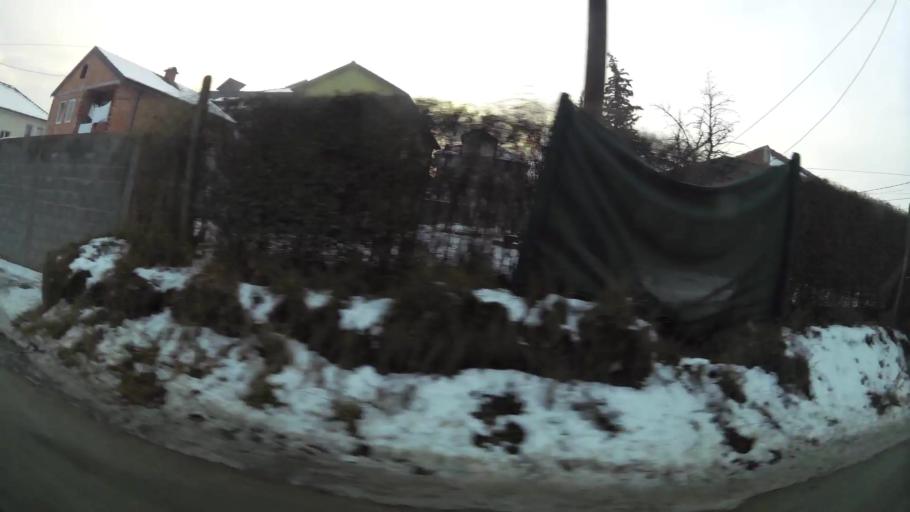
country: MK
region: Suto Orizari
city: Suto Orizare
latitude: 42.0324
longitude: 21.4165
